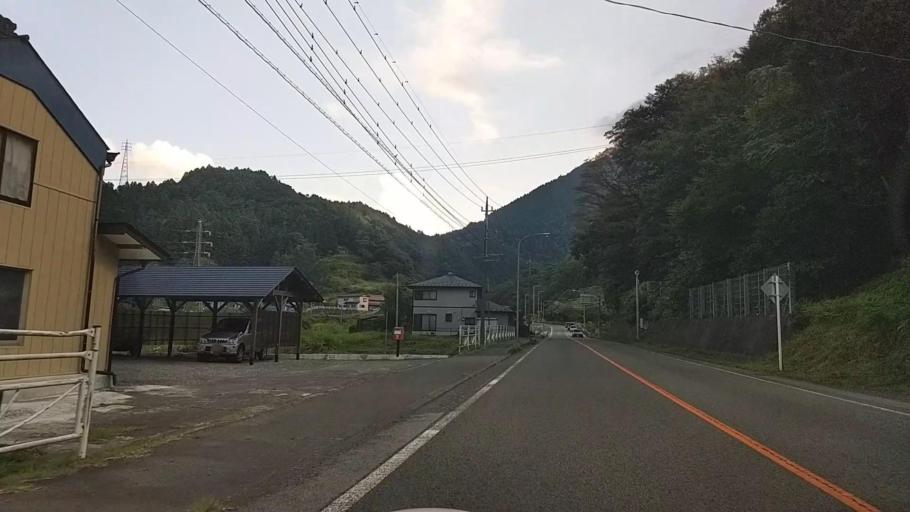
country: JP
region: Shizuoka
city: Fujinomiya
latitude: 35.3330
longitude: 138.4266
